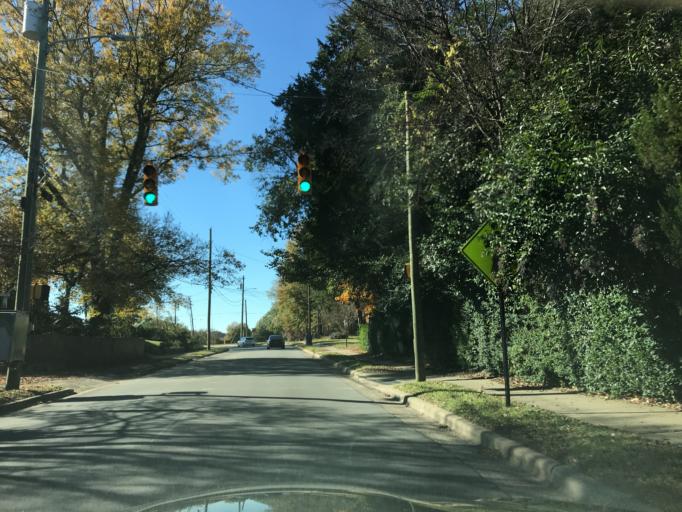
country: US
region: North Carolina
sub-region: Wake County
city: Raleigh
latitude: 35.7912
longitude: -78.6343
